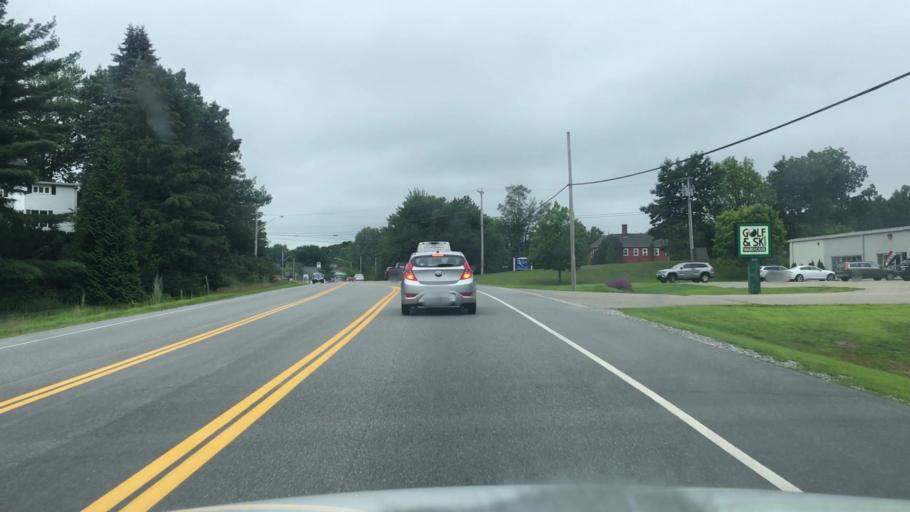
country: US
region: New Hampshire
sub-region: Rockingham County
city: Greenland
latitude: 43.0380
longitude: -70.8378
